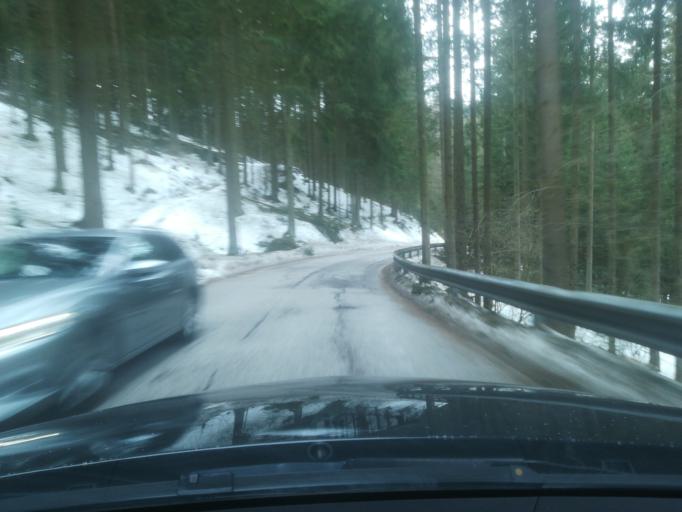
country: AT
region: Upper Austria
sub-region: Politischer Bezirk Perg
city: Perg
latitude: 48.3739
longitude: 14.6304
